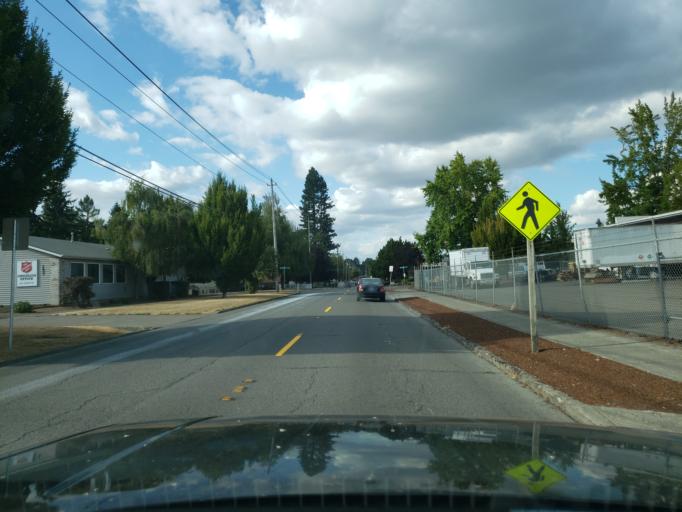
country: US
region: Oregon
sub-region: Marion County
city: Salem
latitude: 44.9579
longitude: -123.0341
